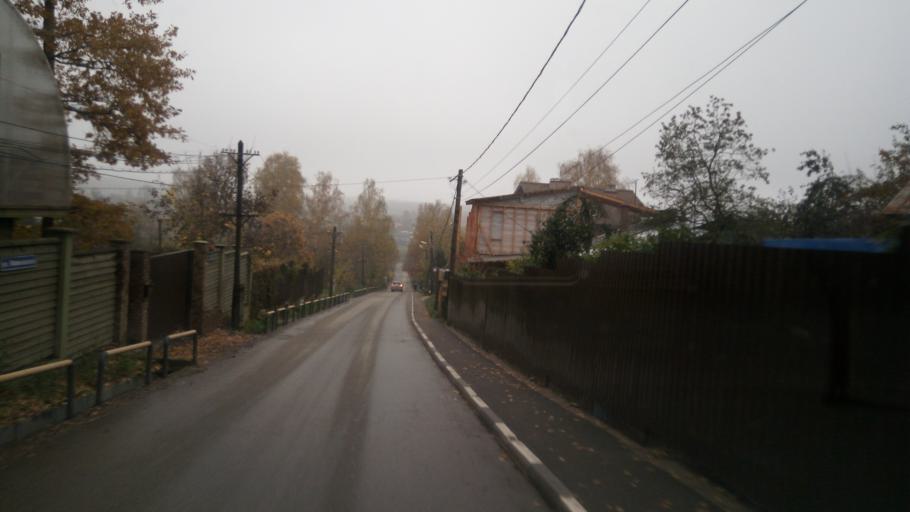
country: RU
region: Moskovskaya
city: Skhodnya
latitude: 55.9398
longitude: 37.2896
